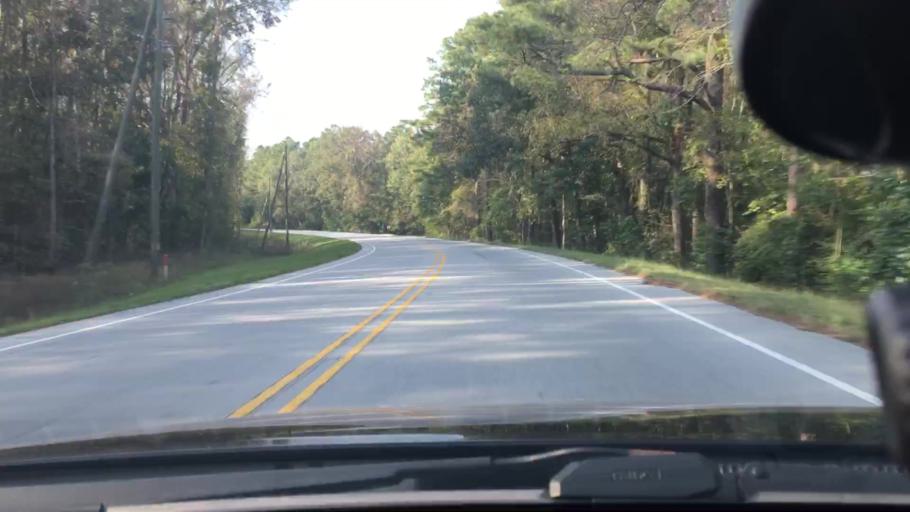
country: US
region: North Carolina
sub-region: Craven County
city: Vanceboro
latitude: 35.2344
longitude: -77.0730
